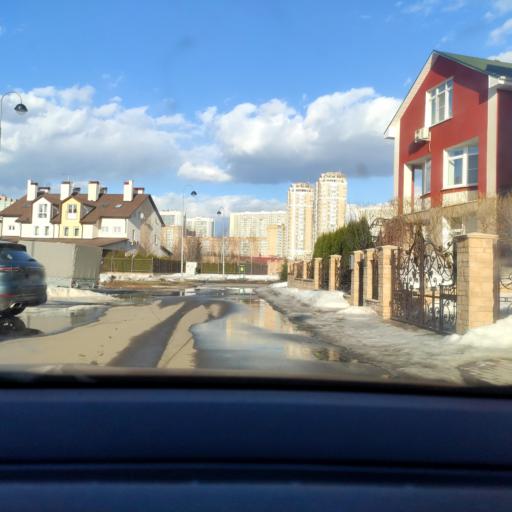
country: RU
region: Moskovskaya
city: Novopodrezkovo
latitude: 55.9060
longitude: 37.3795
